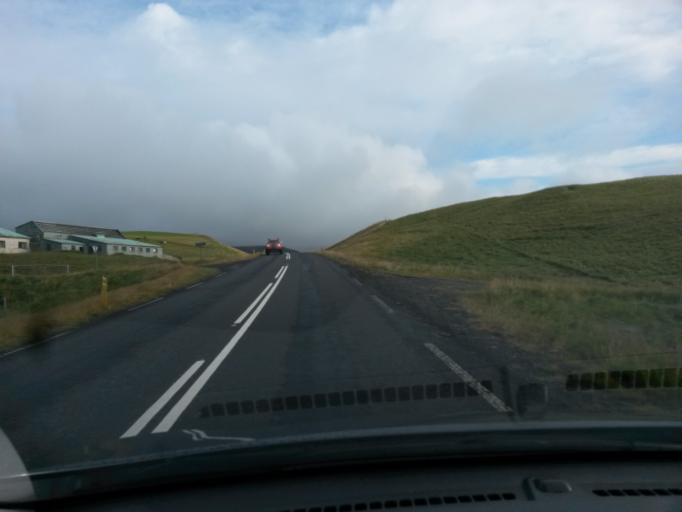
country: IS
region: South
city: Vestmannaeyjar
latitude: 63.4358
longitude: -19.1619
